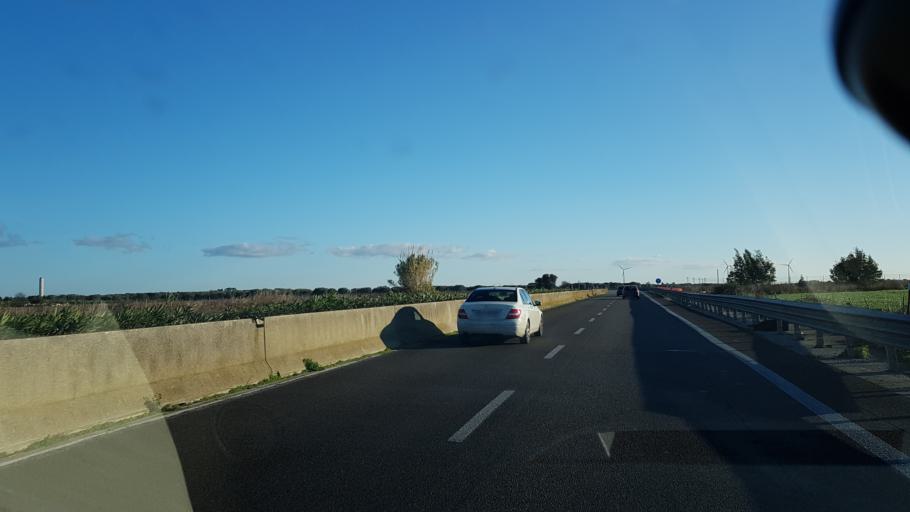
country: IT
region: Apulia
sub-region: Provincia di Brindisi
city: La Rosa
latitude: 40.5873
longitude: 17.9742
